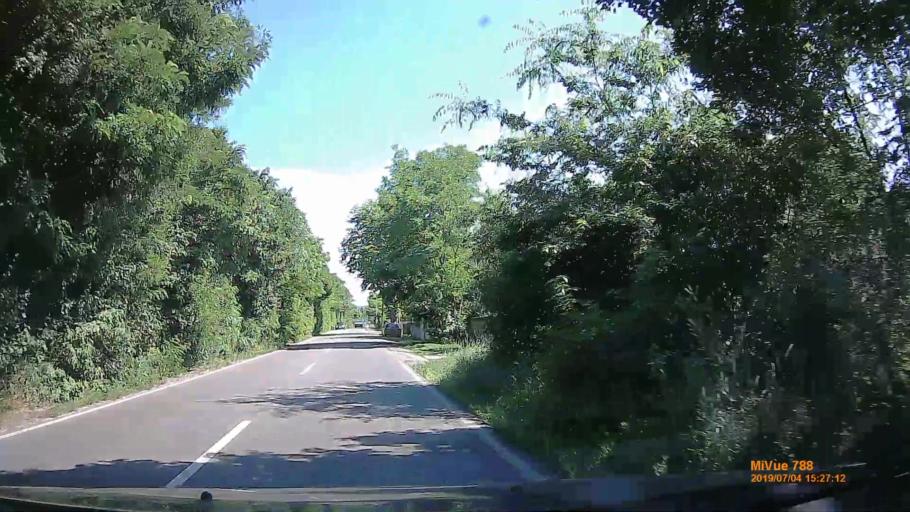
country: HU
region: Komarom-Esztergom
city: Tatabanya
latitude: 47.5450
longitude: 18.3810
